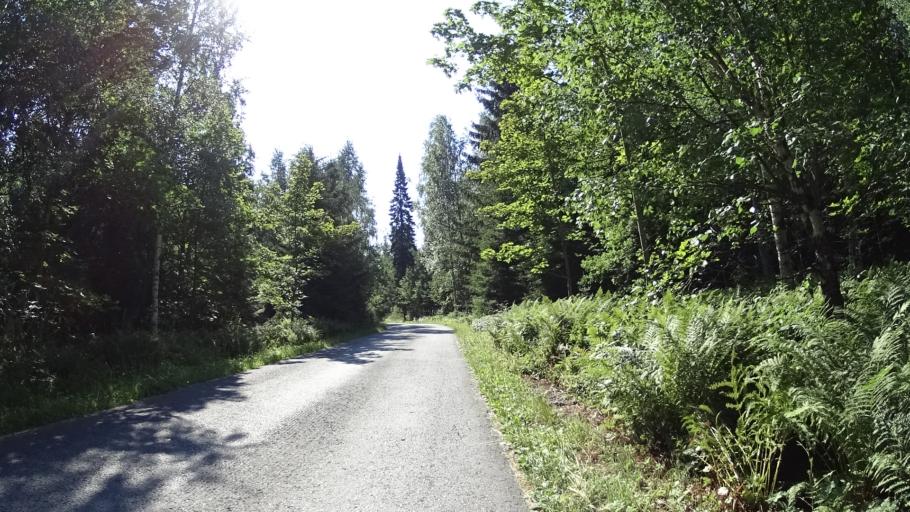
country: FI
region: Haeme
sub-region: Haemeenlinna
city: Haemeenlinna
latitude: 61.0258
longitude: 24.4529
